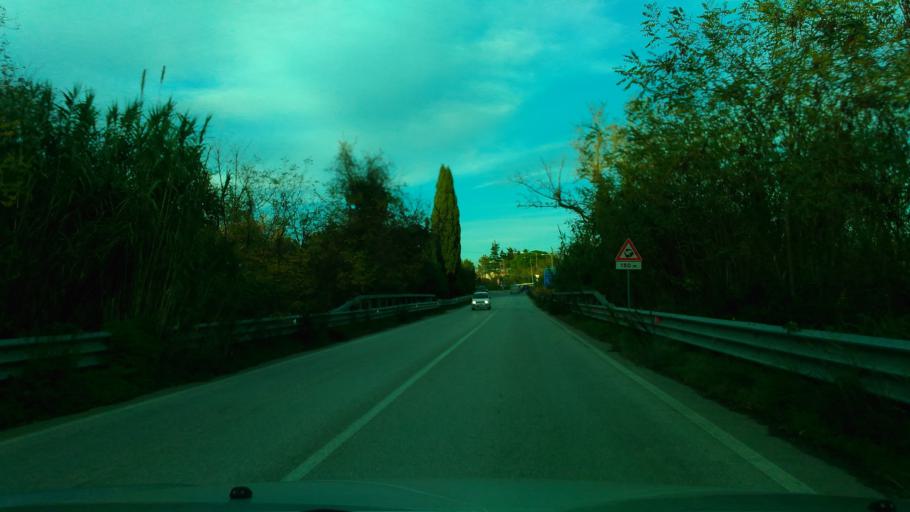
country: IT
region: Tuscany
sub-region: Provincia di Livorno
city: S.P. in Palazzi
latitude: 43.3530
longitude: 10.5062
